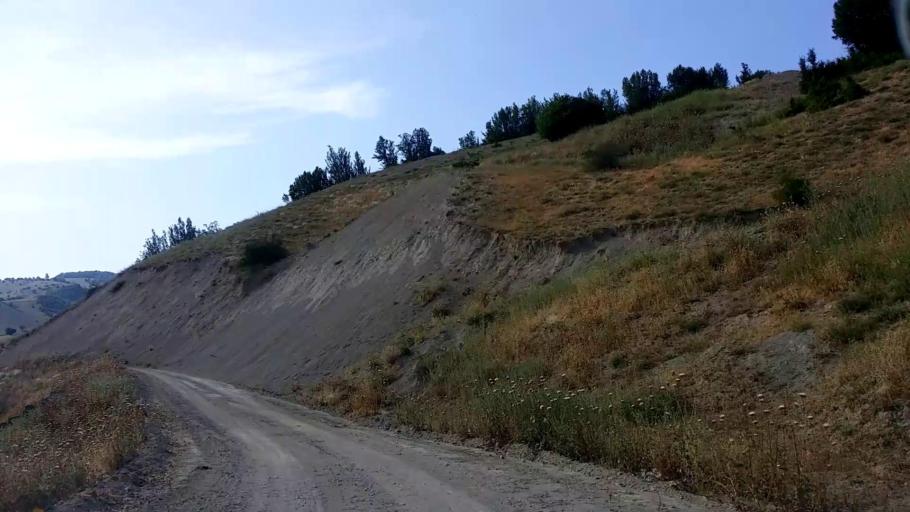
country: IR
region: Mazandaran
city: Chalus
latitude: 36.5463
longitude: 51.2976
